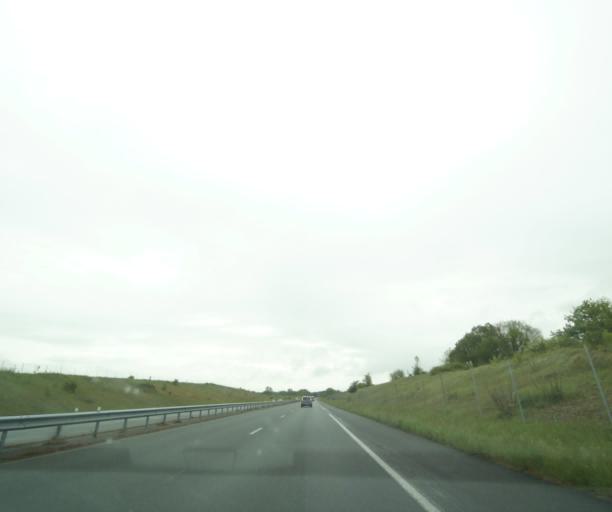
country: FR
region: Poitou-Charentes
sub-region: Departement de la Charente-Maritime
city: Chermignac
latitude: 45.7131
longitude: -0.6898
